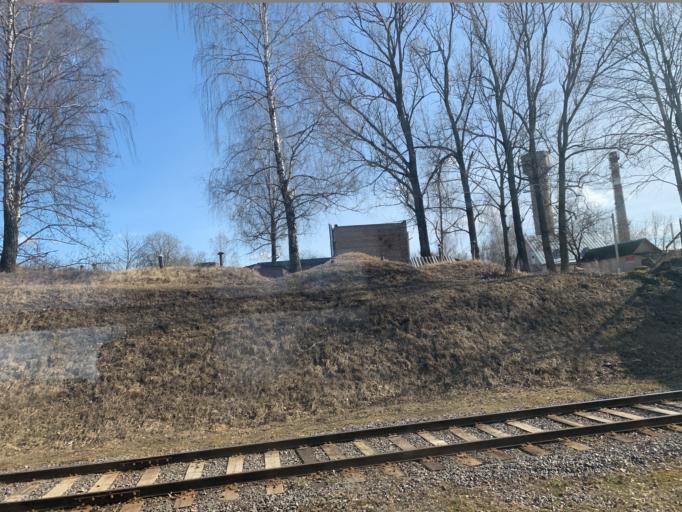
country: BY
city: Fanipol
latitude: 53.7421
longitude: 27.3275
